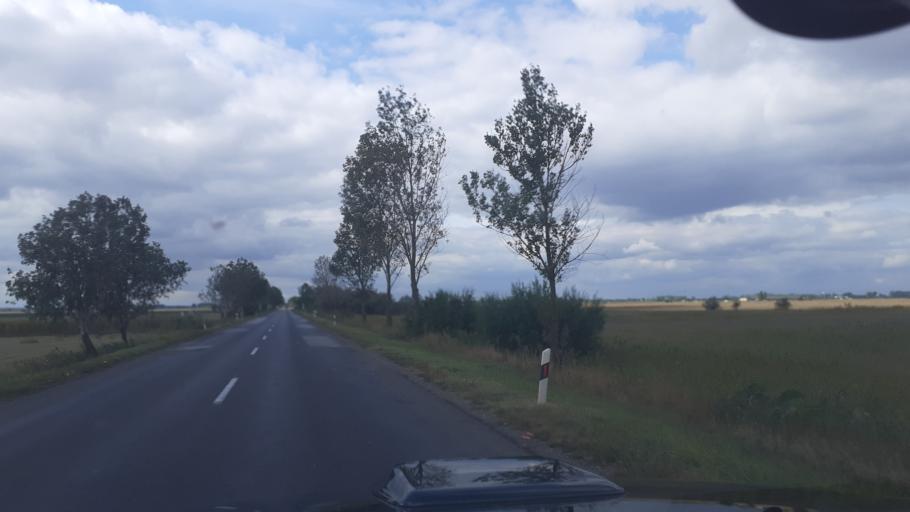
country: HU
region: Bacs-Kiskun
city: Solt
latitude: 46.7979
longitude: 19.0723
